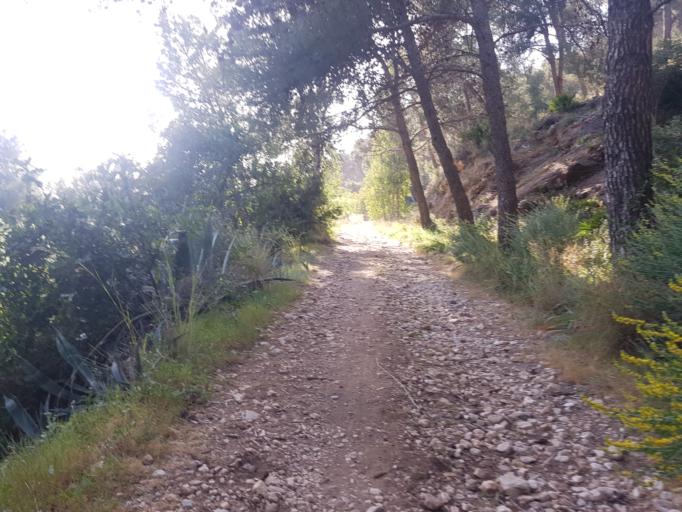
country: ES
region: Andalusia
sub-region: Provincia de Malaga
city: Marbella
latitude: 36.5304
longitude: -4.8785
